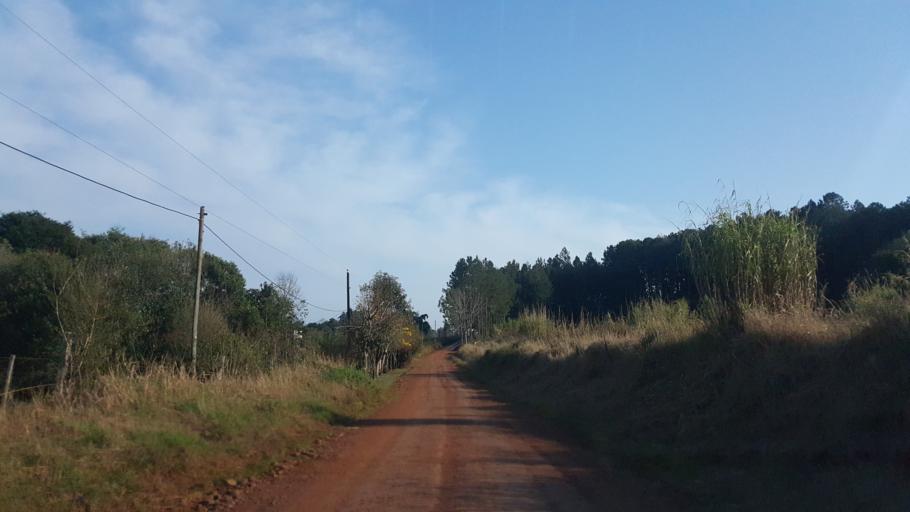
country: AR
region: Misiones
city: Capiovi
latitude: -26.9180
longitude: -55.0620
